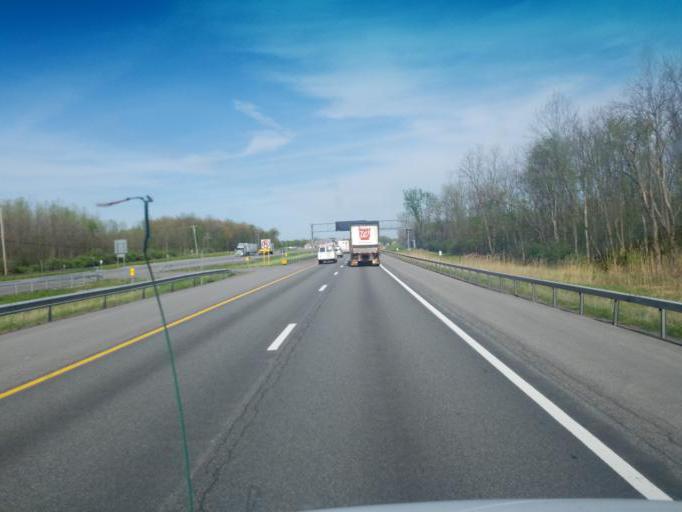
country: US
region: New York
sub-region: Madison County
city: Bolivar
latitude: 43.0956
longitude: -75.8495
